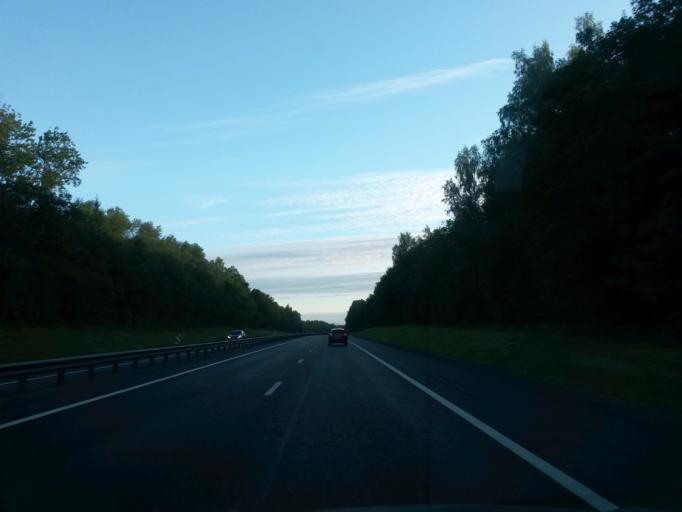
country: RU
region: Moskovskaya
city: Svatkovo
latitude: 56.4020
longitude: 38.3276
